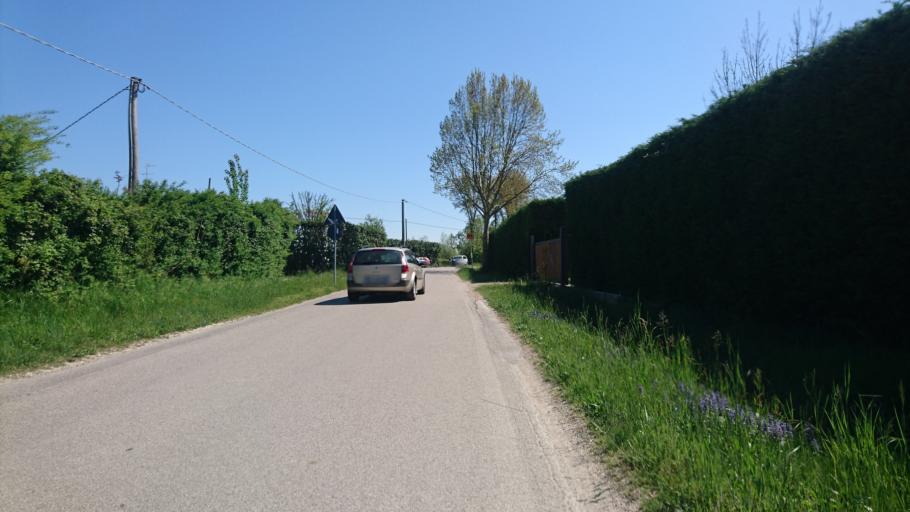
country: IT
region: Veneto
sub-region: Provincia di Treviso
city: Conscio
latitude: 45.5885
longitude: 12.2781
